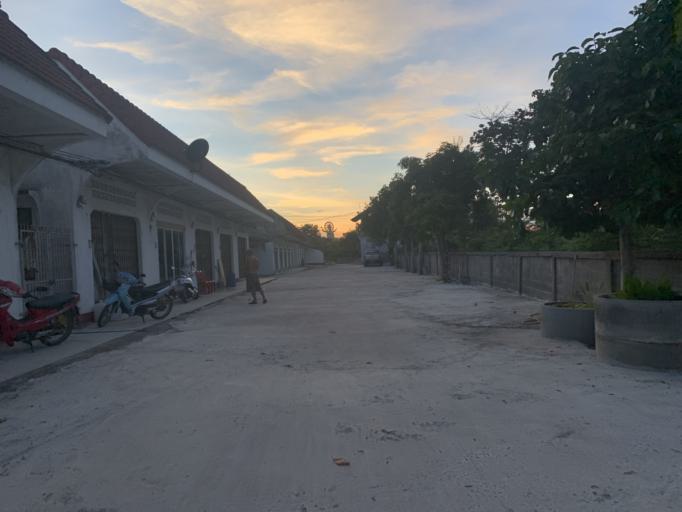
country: TH
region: Surat Thani
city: Ko Samui
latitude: 9.5690
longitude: 100.0632
